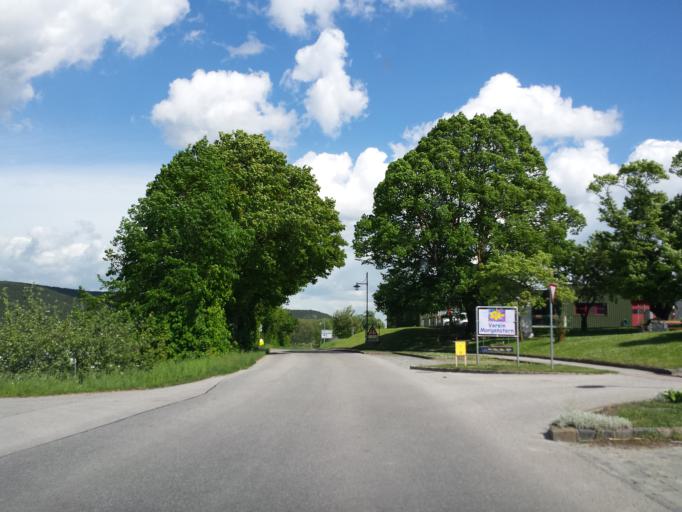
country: AT
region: Lower Austria
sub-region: Politischer Bezirk Wiener Neustadt
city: Markt Piesting
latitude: 47.8724
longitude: 16.1382
